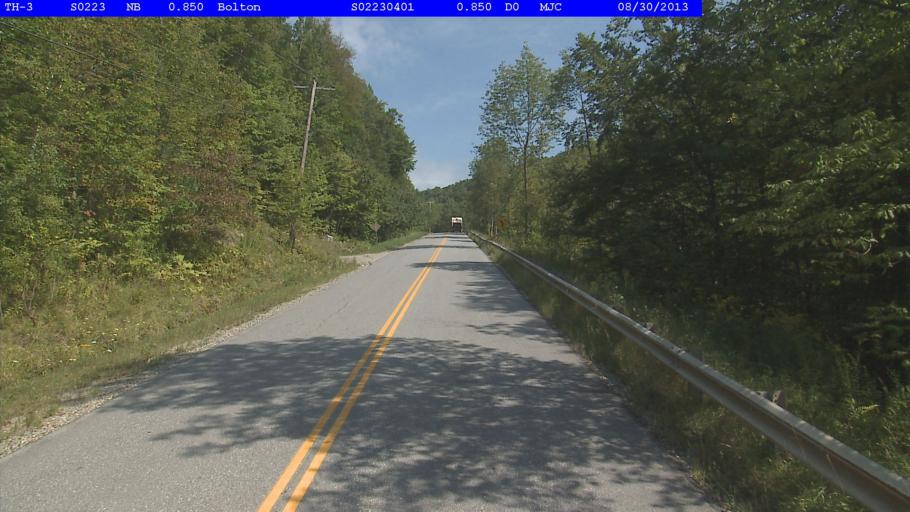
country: US
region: Vermont
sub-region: Washington County
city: Waterbury
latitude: 44.3829
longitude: -72.8745
